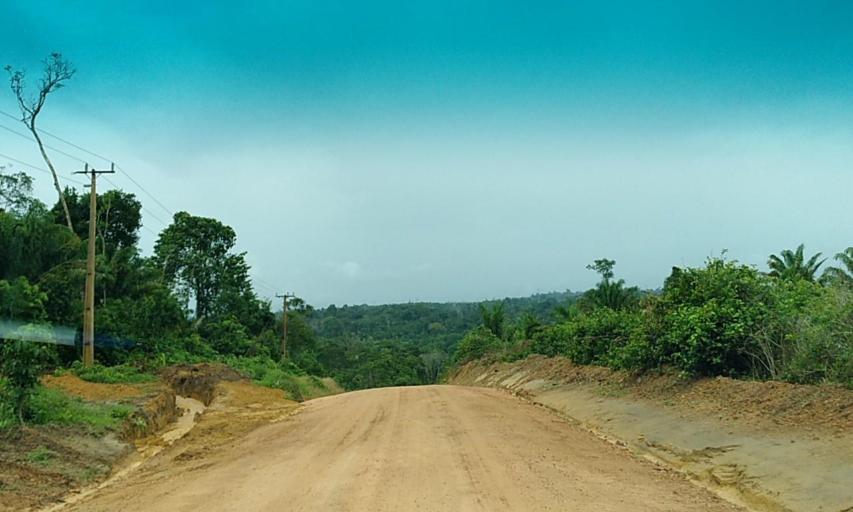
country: BR
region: Para
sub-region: Senador Jose Porfirio
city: Senador Jose Porfirio
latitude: -3.0599
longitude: -51.6554
